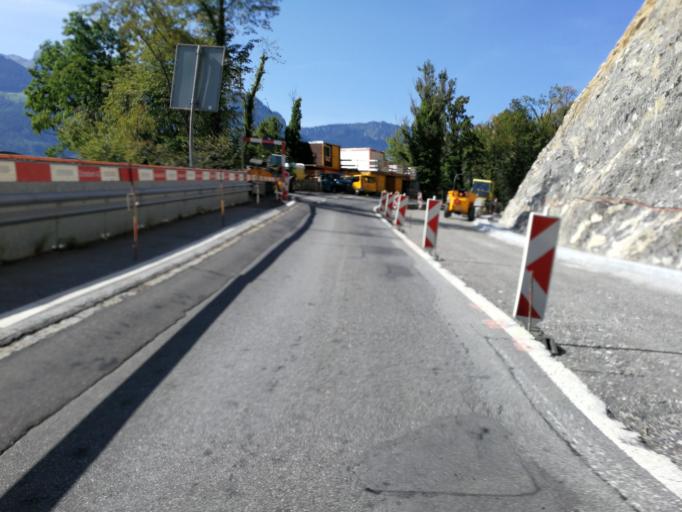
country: CH
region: Lucerne
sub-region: Lucerne-Land District
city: Vitznau
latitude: 46.9917
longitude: 8.4996
